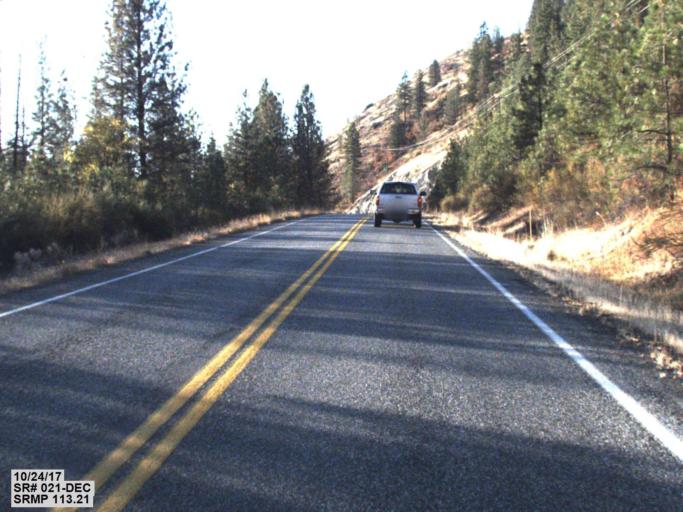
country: US
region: Washington
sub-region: Okanogan County
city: Coulee Dam
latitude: 48.0319
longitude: -118.6745
